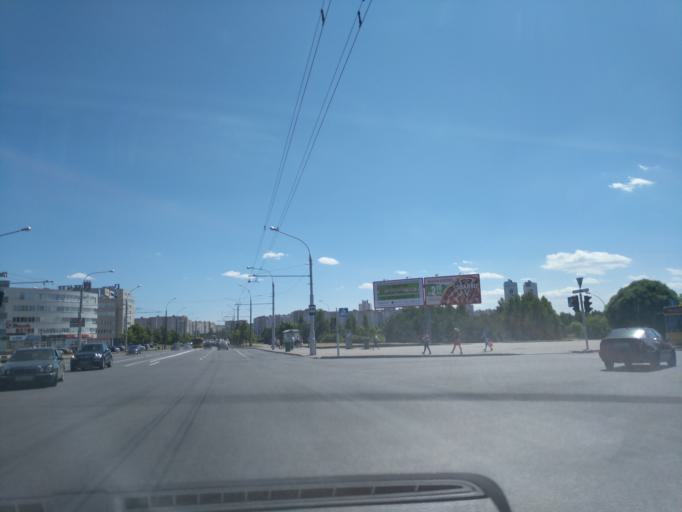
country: BY
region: Minsk
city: Borovlyany
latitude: 53.9478
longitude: 27.6801
